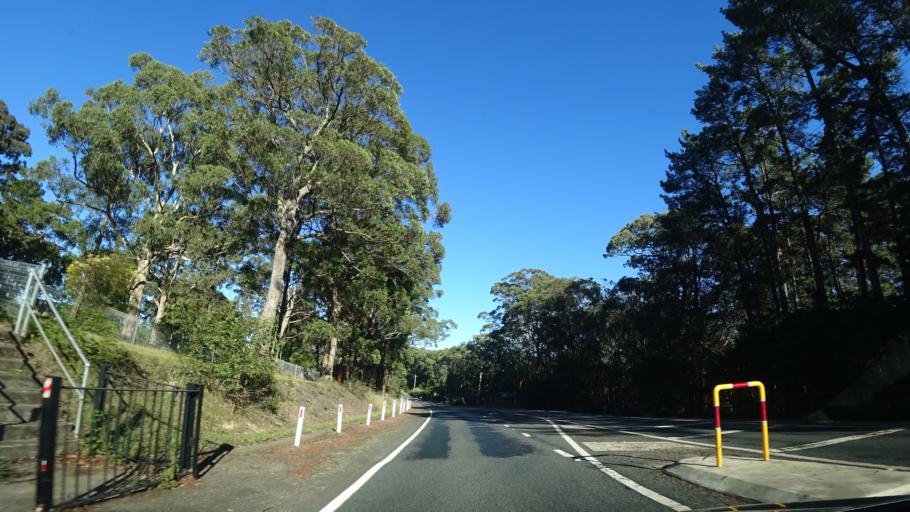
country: AU
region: New South Wales
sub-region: Blue Mountains Municipality
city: Hazelbrook
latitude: -33.4969
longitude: 150.5180
